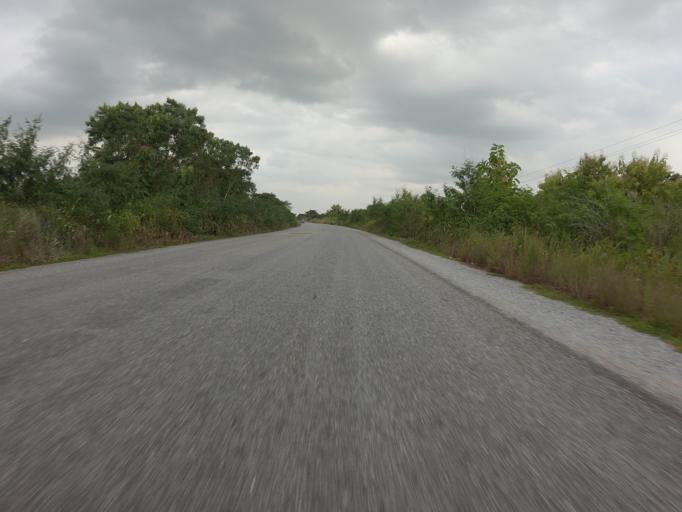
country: GH
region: Volta
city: Ho
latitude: 6.4745
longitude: 0.4955
